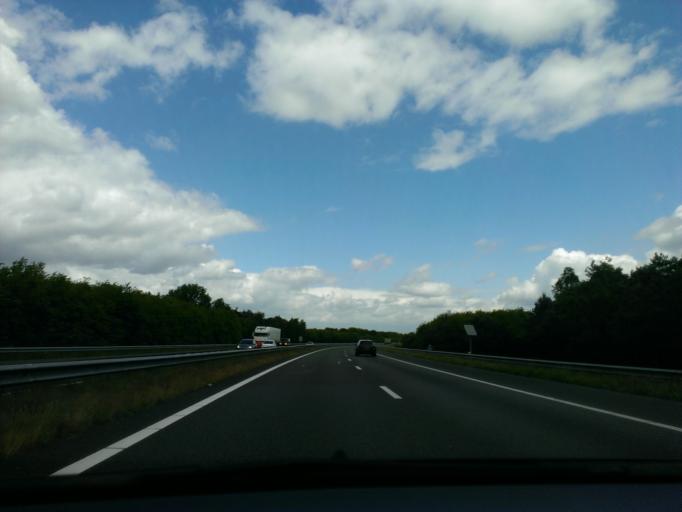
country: NL
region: Limburg
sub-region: Gemeente Venray
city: Venray
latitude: 51.5519
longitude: 5.9918
